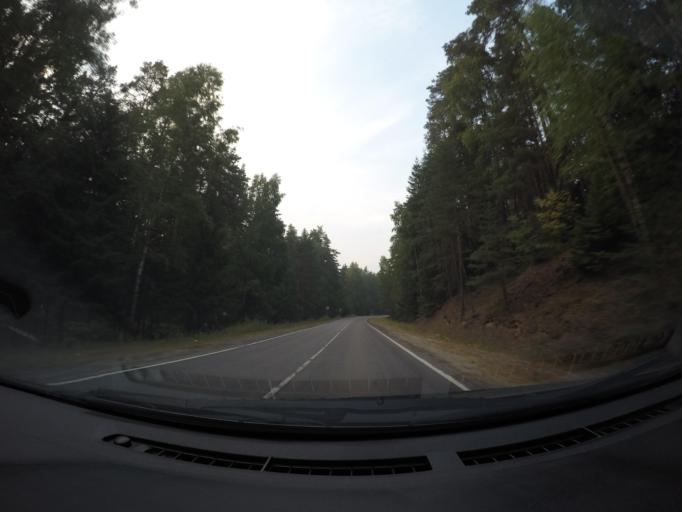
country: RU
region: Moskovskaya
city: Imeni Tsyurupy
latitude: 55.5055
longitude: 38.7148
